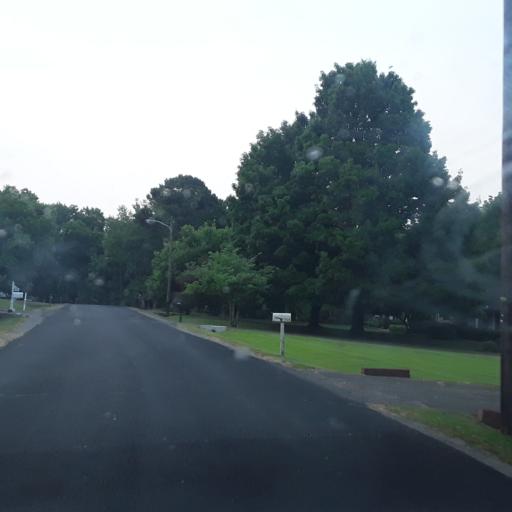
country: US
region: Tennessee
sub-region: Williamson County
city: Brentwood
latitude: 36.0570
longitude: -86.7673
